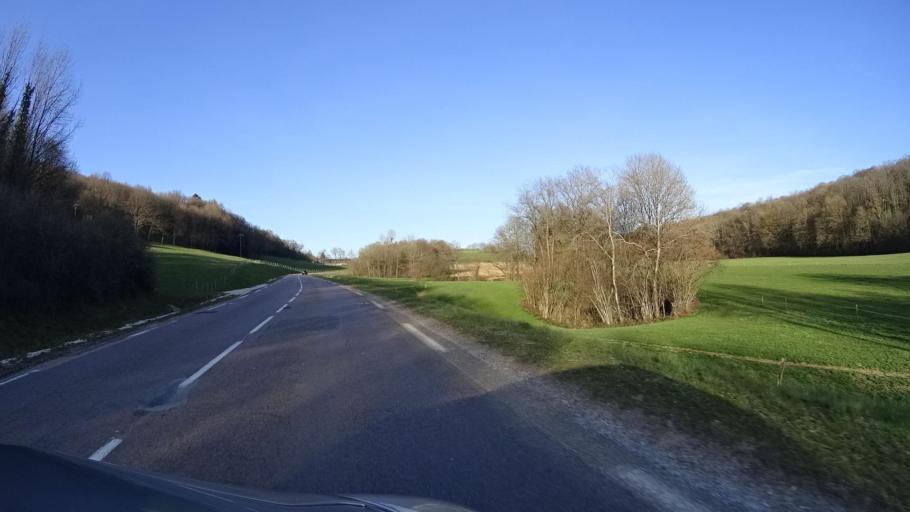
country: FR
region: Franche-Comte
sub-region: Departement du Doubs
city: Morre
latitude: 47.2044
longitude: 6.0452
